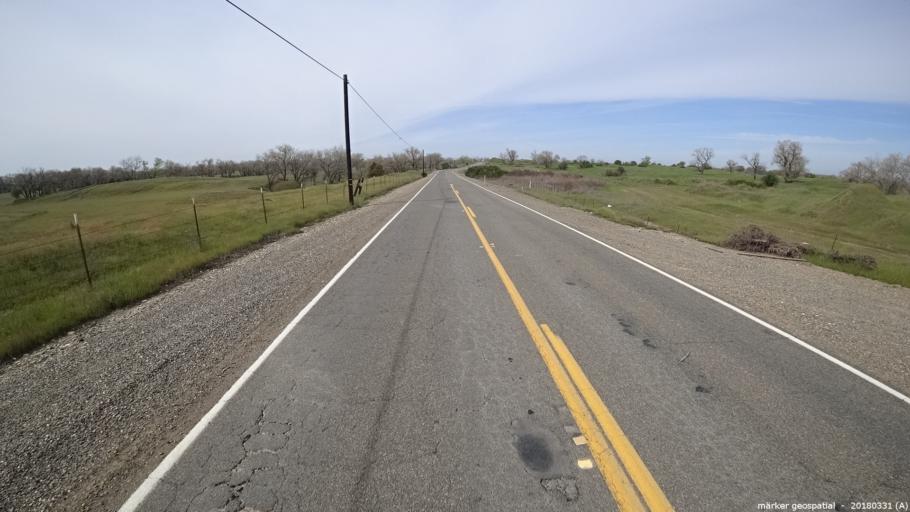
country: US
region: California
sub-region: Sacramento County
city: Gold River
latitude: 38.5947
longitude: -121.1877
